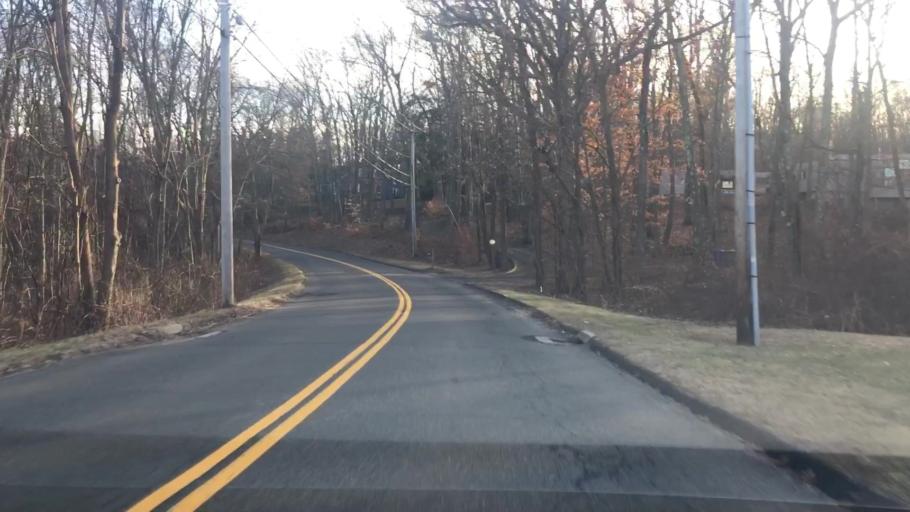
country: US
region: Connecticut
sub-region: Middlesex County
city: Durham
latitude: 41.5142
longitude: -72.6487
